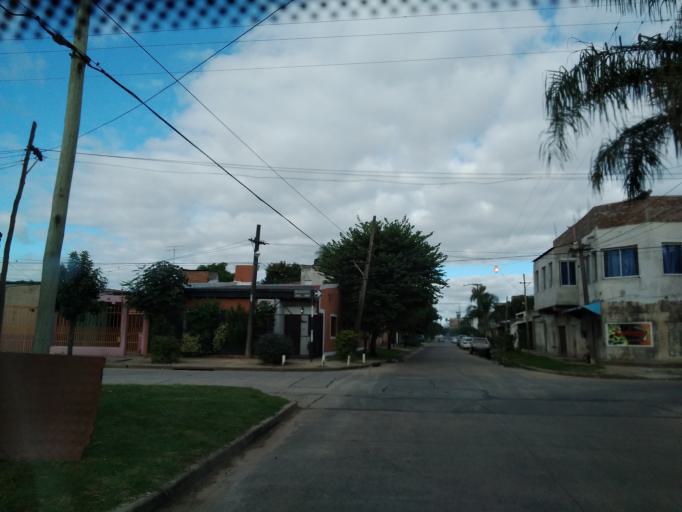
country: AR
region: Corrientes
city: Corrientes
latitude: -27.4761
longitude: -58.8109
